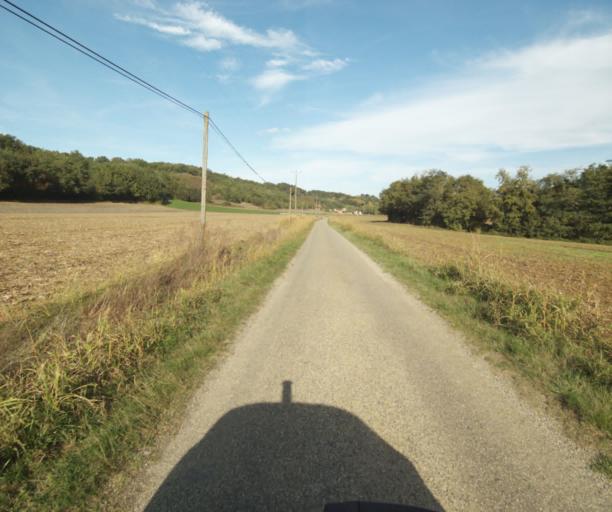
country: FR
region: Midi-Pyrenees
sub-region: Departement du Tarn-et-Garonne
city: Saint-Porquier
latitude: 43.9383
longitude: 1.1493
